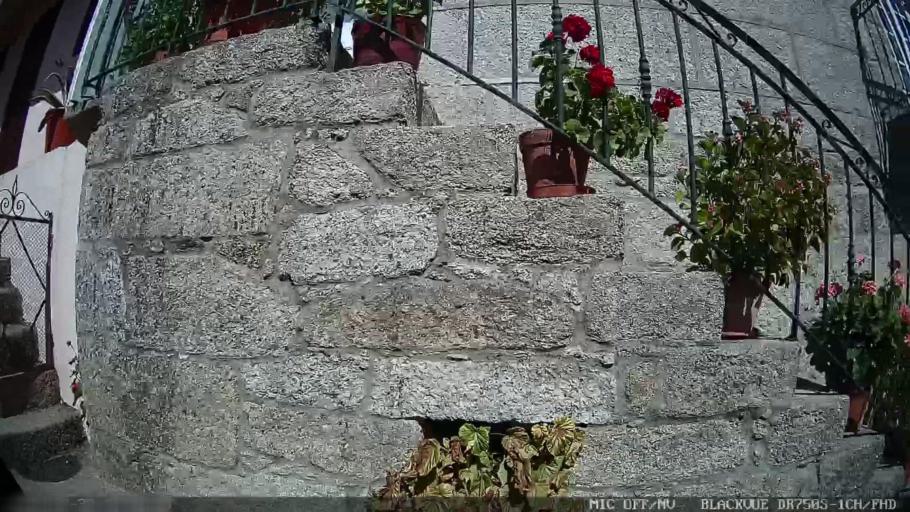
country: PT
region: Vila Real
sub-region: Murca
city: Murca
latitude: 41.3273
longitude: -7.4886
